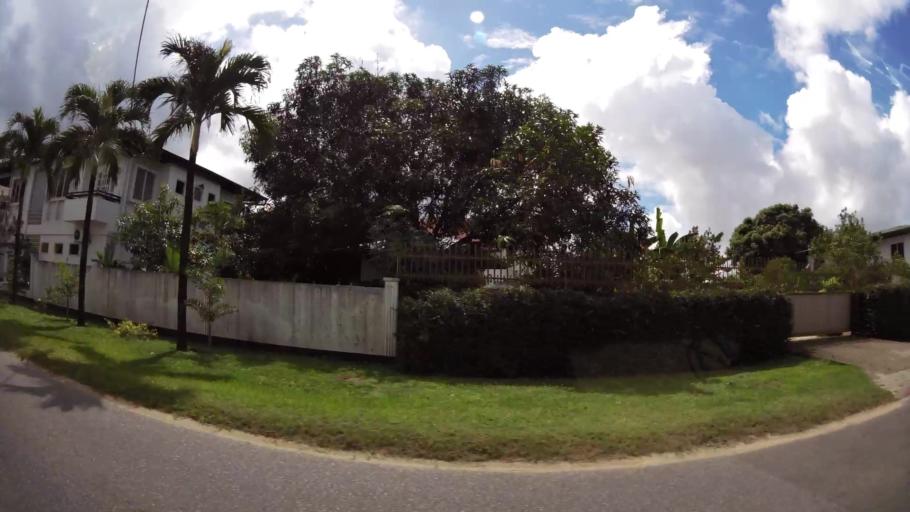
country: SR
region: Paramaribo
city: Paramaribo
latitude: 5.8356
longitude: -55.1925
